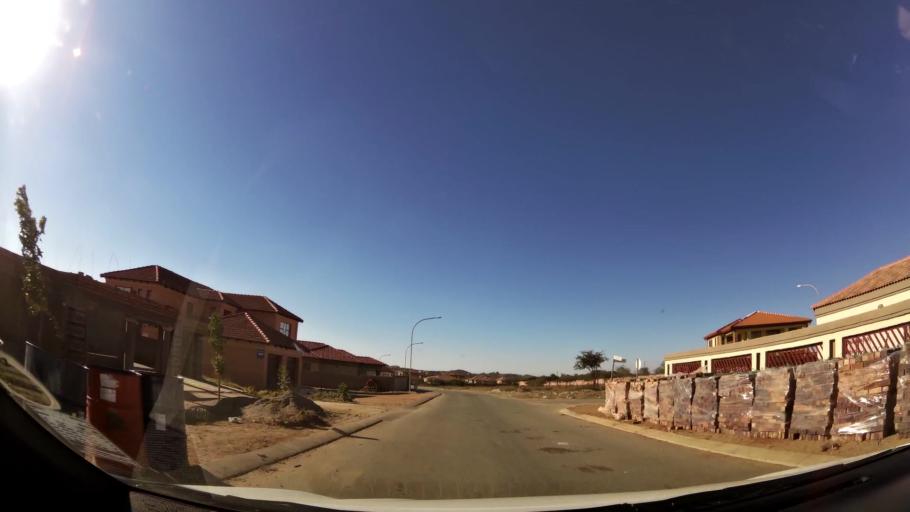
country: ZA
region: Limpopo
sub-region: Capricorn District Municipality
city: Polokwane
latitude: -23.9111
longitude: 29.5077
